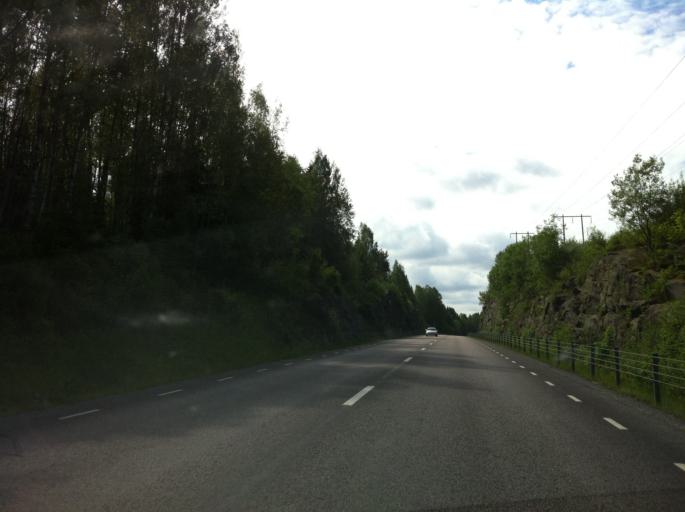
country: SE
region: Vaermland
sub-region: Karlstads Kommun
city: Valberg
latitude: 59.3984
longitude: 13.1807
